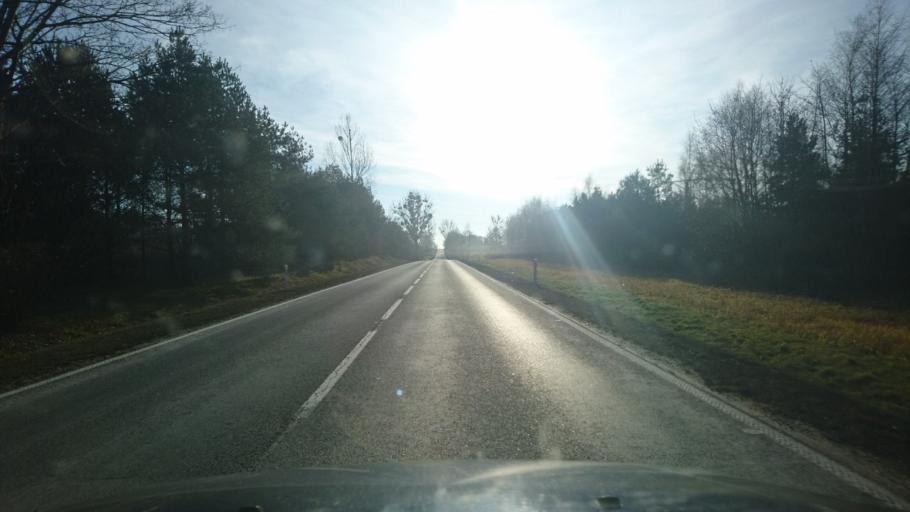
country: PL
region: Opole Voivodeship
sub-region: Powiat oleski
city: Dalachow
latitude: 51.0697
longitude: 18.6018
